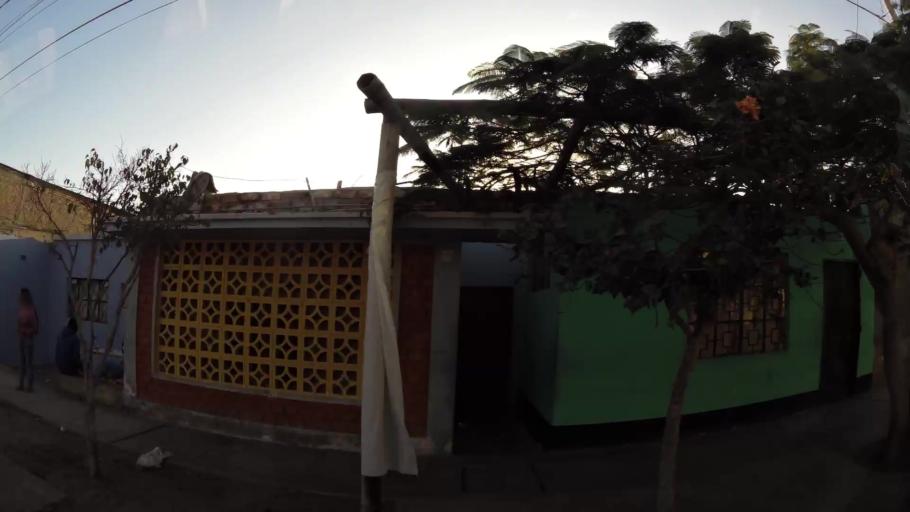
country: PE
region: Ica
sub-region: Provincia de Pisco
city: Villa Tupac Amaru
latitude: -13.7124
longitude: -76.1522
